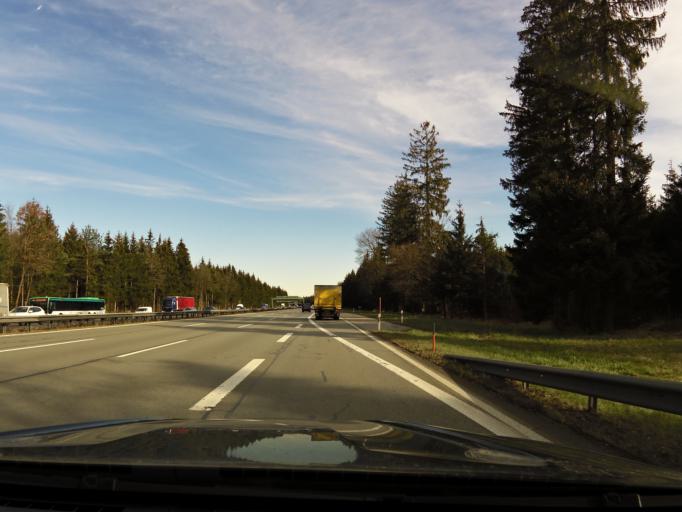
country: DE
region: Bavaria
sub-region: Upper Bavaria
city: Brunnthal
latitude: 47.9834
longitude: 11.6831
